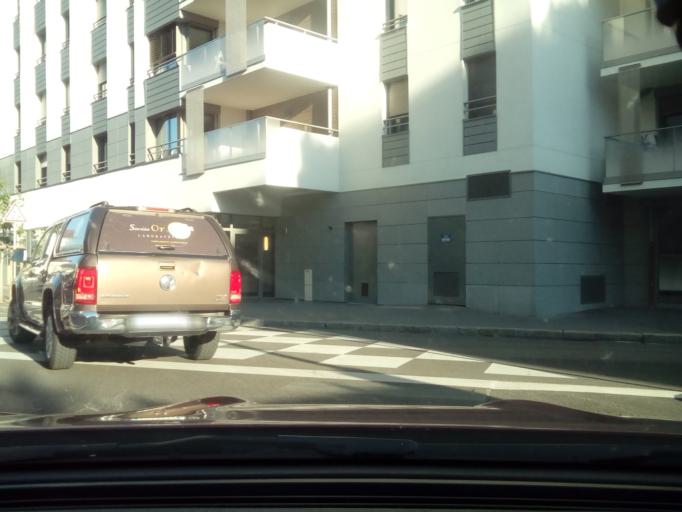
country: FR
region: Rhone-Alpes
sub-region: Departement de la Haute-Savoie
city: Annecy
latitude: 45.9007
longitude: 6.1204
